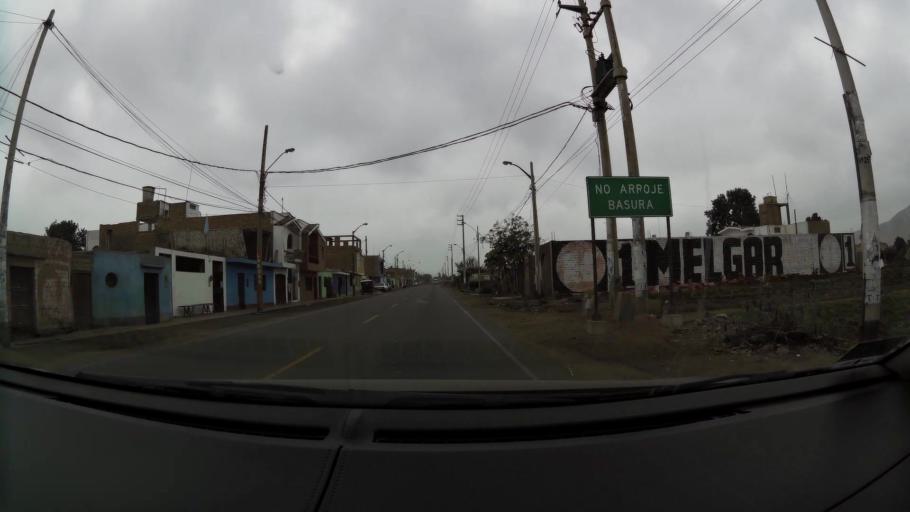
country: PE
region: Lima
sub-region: Provincia de Huaral
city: Chancay
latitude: -11.5265
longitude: -77.2480
